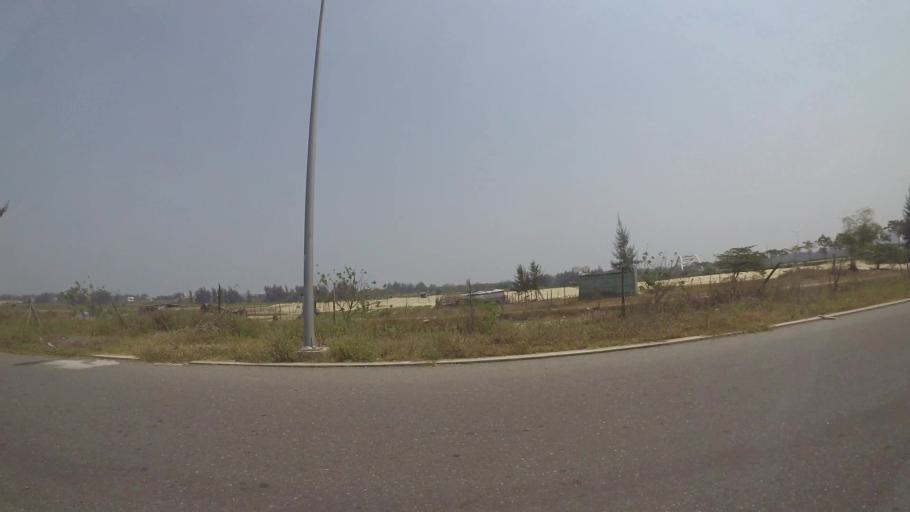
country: VN
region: Da Nang
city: Ngu Hanh Son
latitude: 15.9787
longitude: 108.2636
